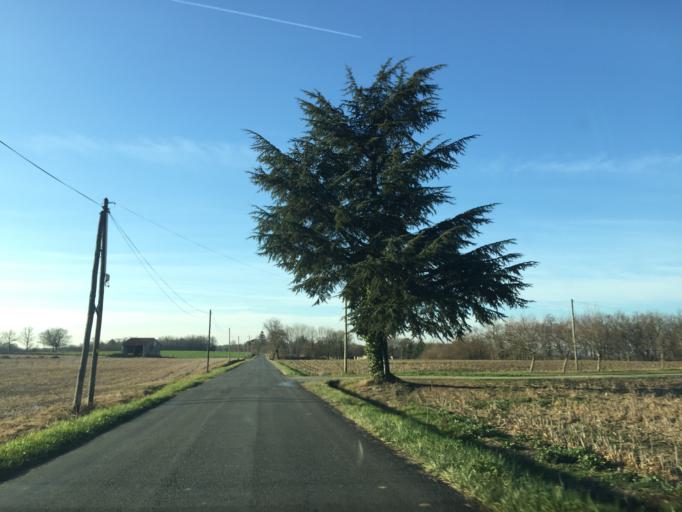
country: FR
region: Aquitaine
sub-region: Departement de la Dordogne
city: Riberac
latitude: 45.2009
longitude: 0.3282
